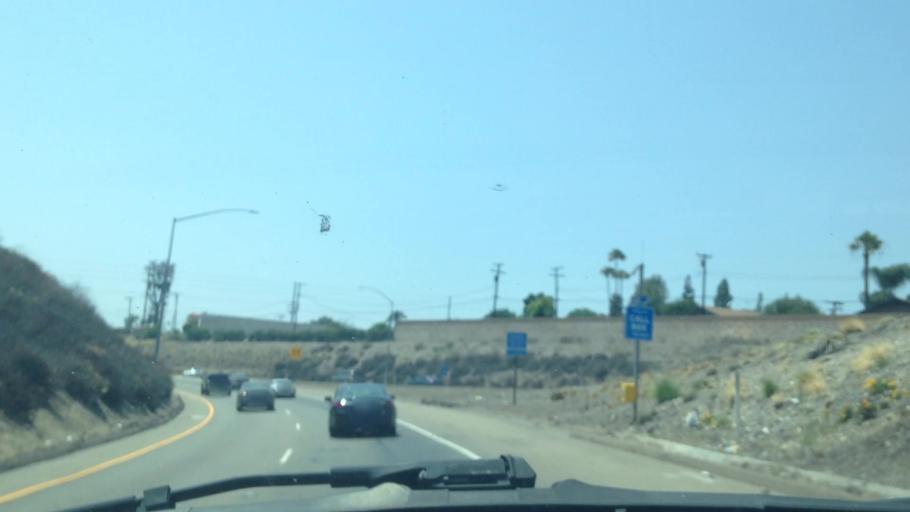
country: US
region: California
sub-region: Orange County
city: Orange
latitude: 33.7777
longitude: -117.8326
